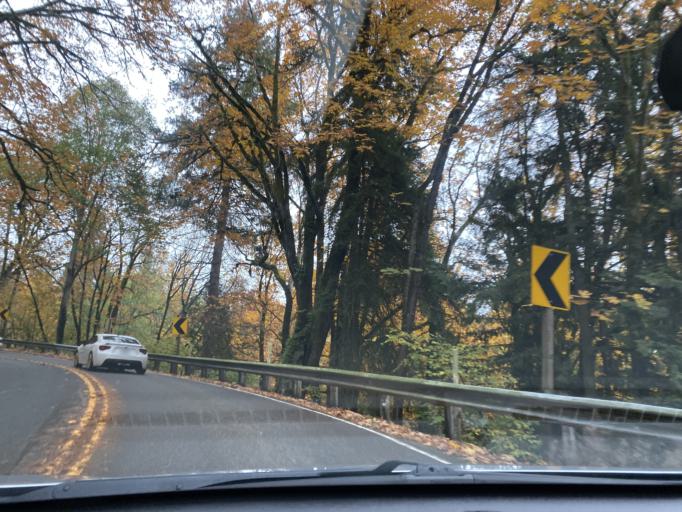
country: US
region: Washington
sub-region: King County
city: Lea Hill
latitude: 47.2995
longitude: -122.1706
